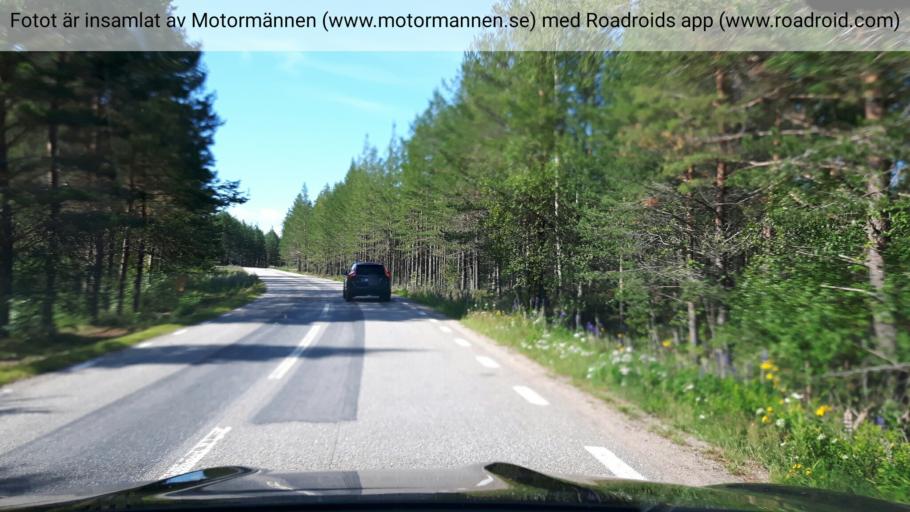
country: SE
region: Gaevleborg
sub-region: Ljusdals Kommun
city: Farila
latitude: 61.7934
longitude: 15.6454
